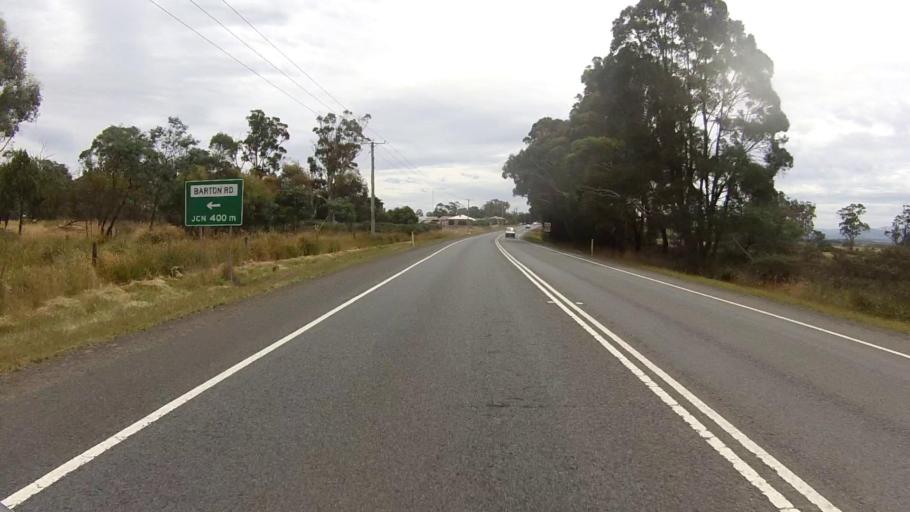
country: AU
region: Tasmania
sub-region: Northern Midlands
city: Evandale
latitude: -41.7632
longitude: 147.3539
